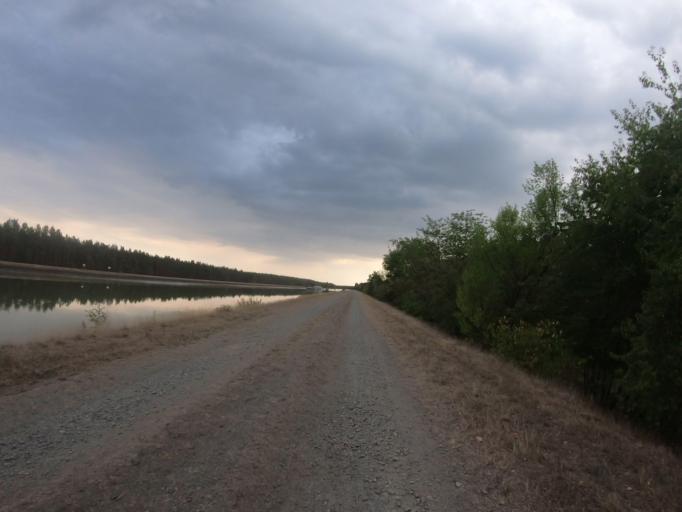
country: DE
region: Lower Saxony
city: Sassenburg
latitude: 52.5492
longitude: 10.6593
